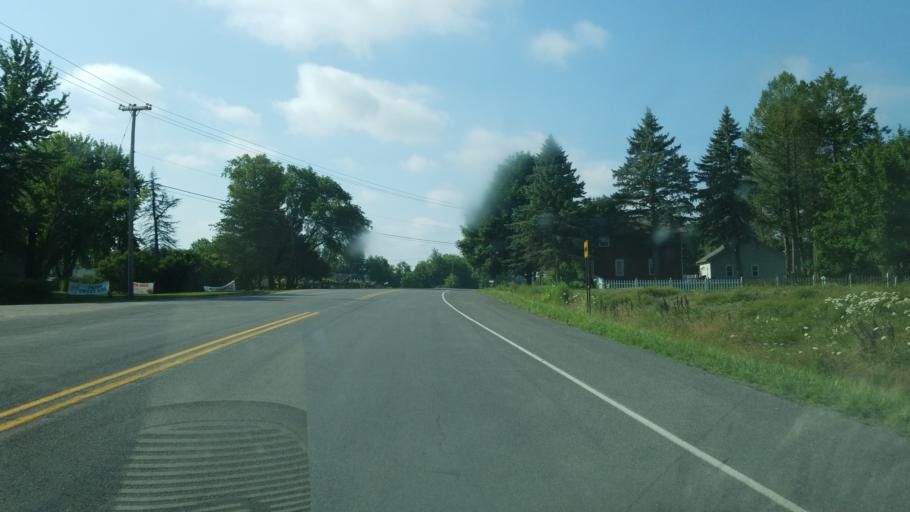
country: US
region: Michigan
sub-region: Kent County
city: Northview
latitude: 43.1010
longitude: -85.6392
